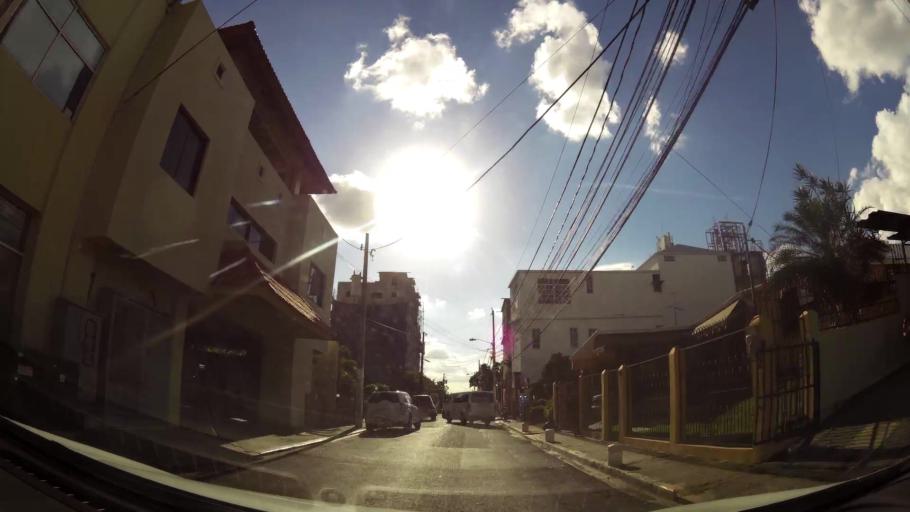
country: DO
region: Santiago
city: Santiago de los Caballeros
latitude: 19.4619
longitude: -70.6890
